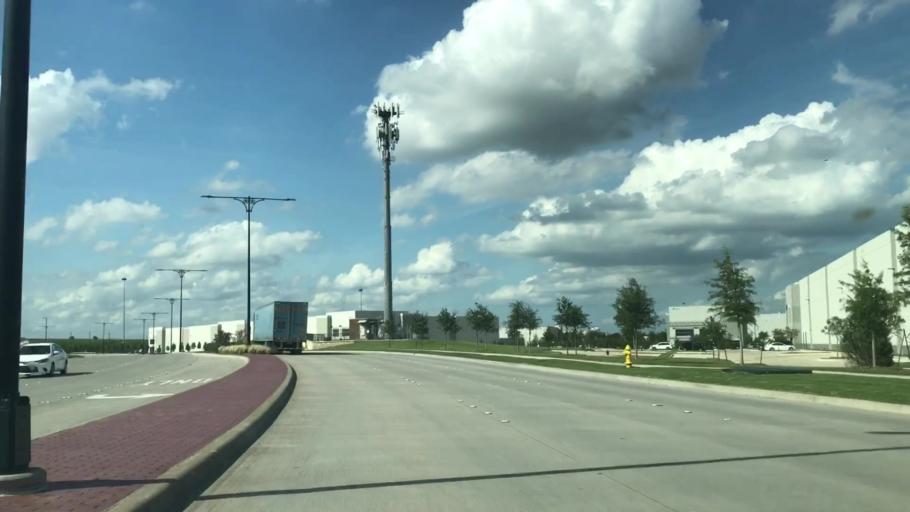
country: US
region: Texas
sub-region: Dallas County
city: Coppell
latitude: 32.9759
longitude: -97.0152
